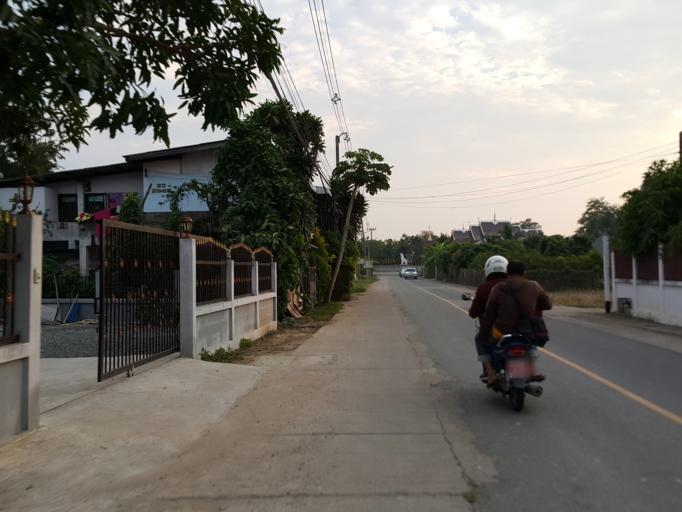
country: TH
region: Chiang Mai
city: San Sai
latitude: 18.8819
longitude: 99.1256
